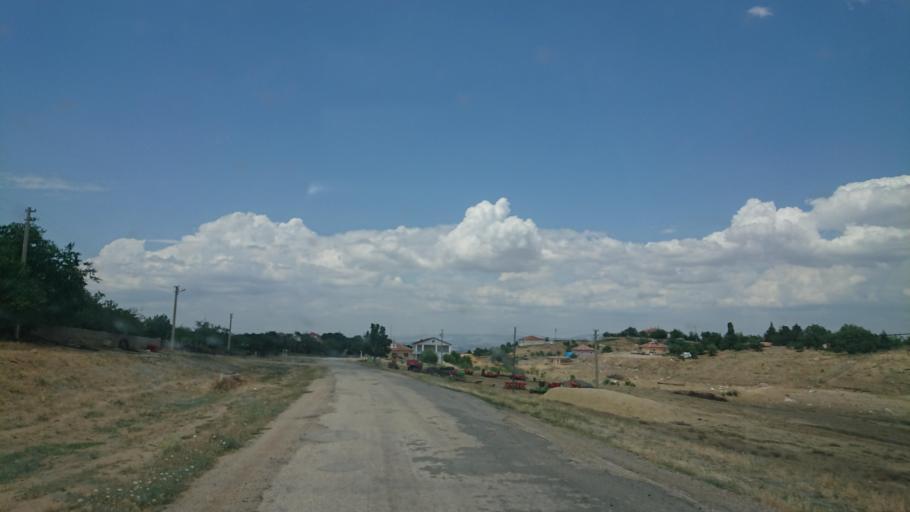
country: TR
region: Aksaray
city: Sariyahsi
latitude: 38.9538
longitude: 33.8832
